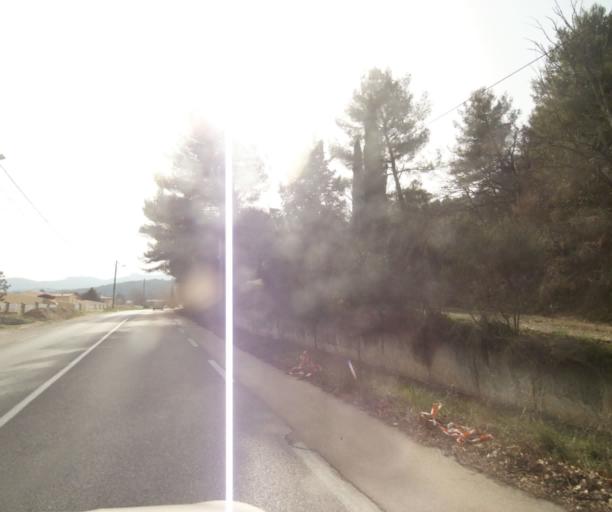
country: FR
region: Provence-Alpes-Cote d'Azur
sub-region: Departement des Bouches-du-Rhone
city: Gardanne
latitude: 43.4432
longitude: 5.4579
